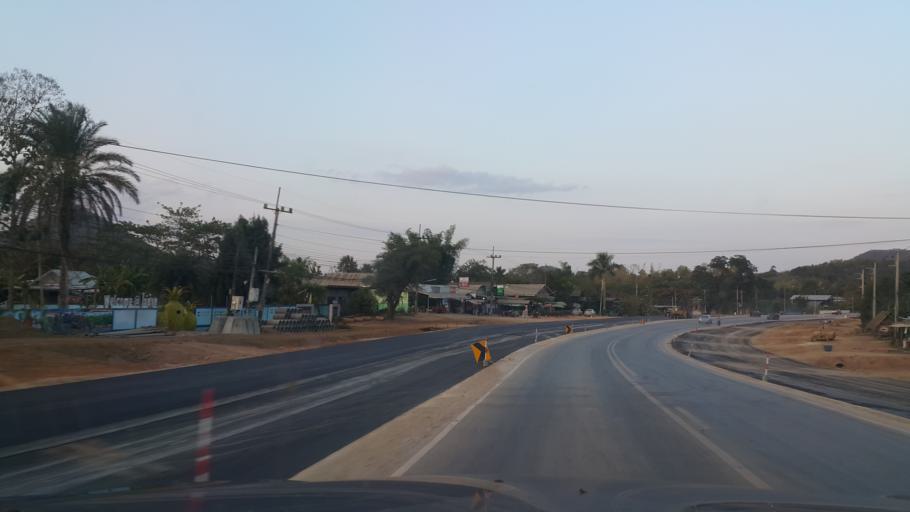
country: TH
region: Loei
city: Loei
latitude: 17.4892
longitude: 101.6851
